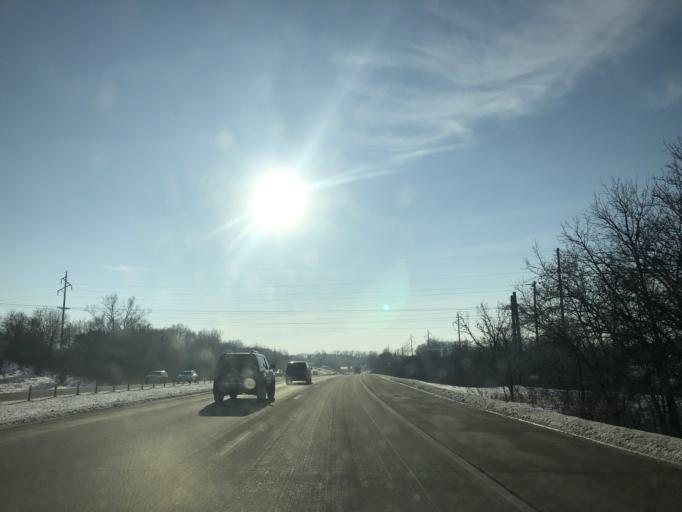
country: US
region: Minnesota
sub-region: Ramsey County
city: Shoreview
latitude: 45.0727
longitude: -93.1695
